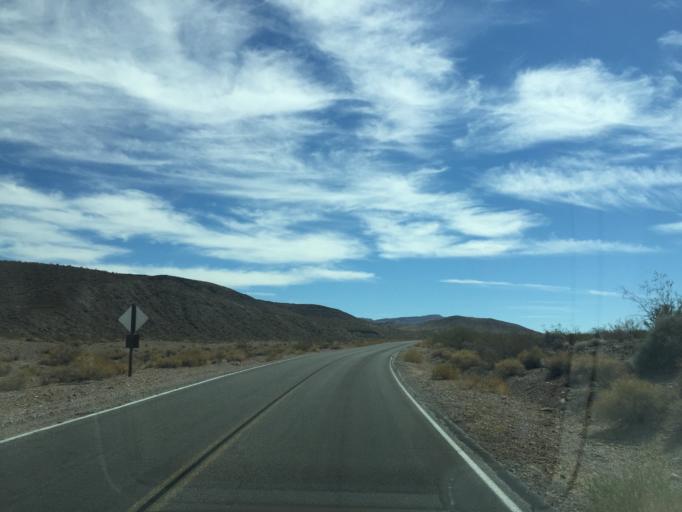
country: US
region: Nevada
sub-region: Nye County
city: Beatty
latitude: 36.2745
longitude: -116.6659
